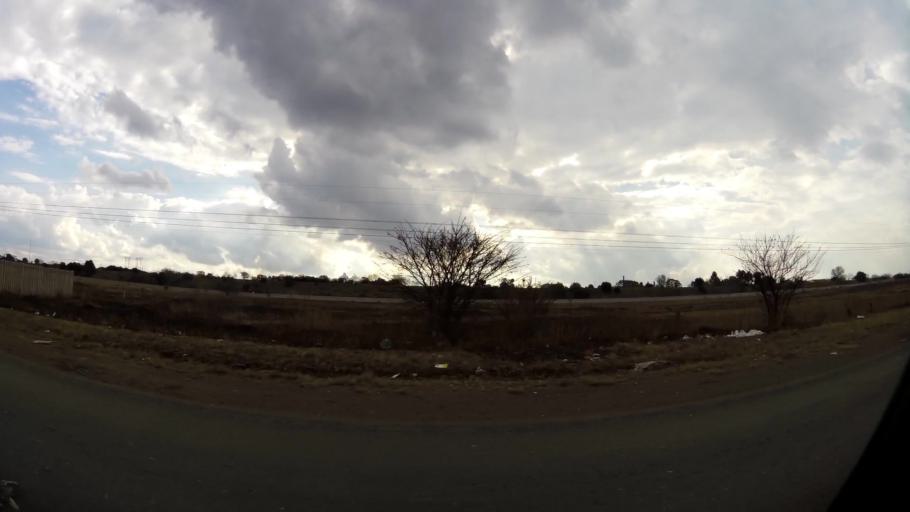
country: ZA
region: Gauteng
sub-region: Sedibeng District Municipality
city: Vanderbijlpark
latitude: -26.6653
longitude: 27.8419
